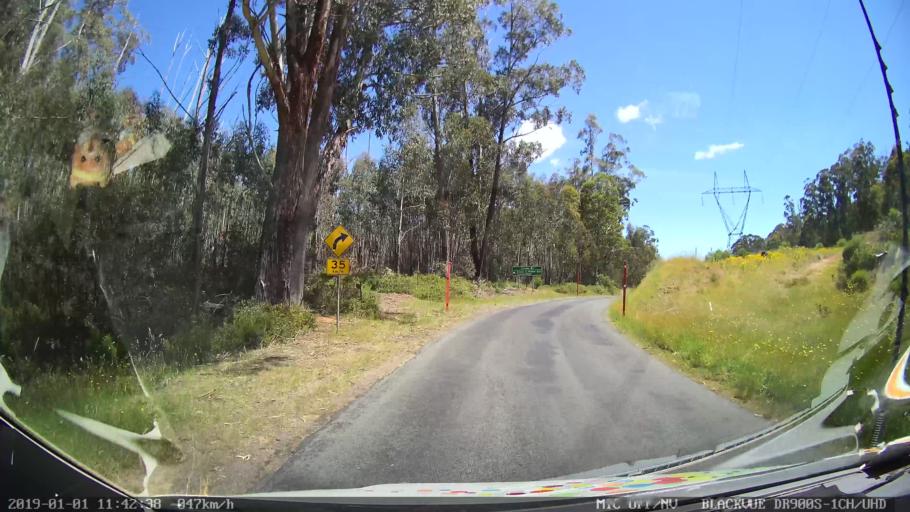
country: AU
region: New South Wales
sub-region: Snowy River
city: Jindabyne
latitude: -35.9078
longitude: 148.3842
